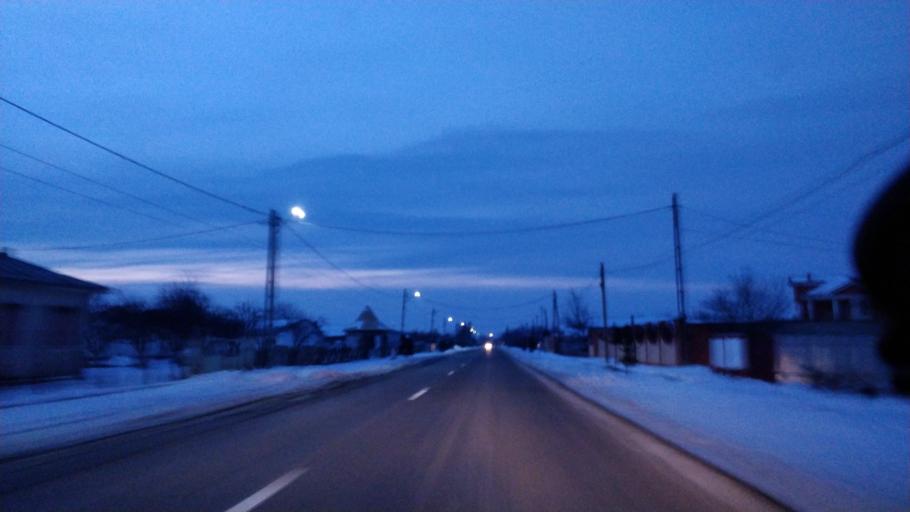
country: RO
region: Vrancea
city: Vulturu de Sus
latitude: 45.6115
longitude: 27.4389
